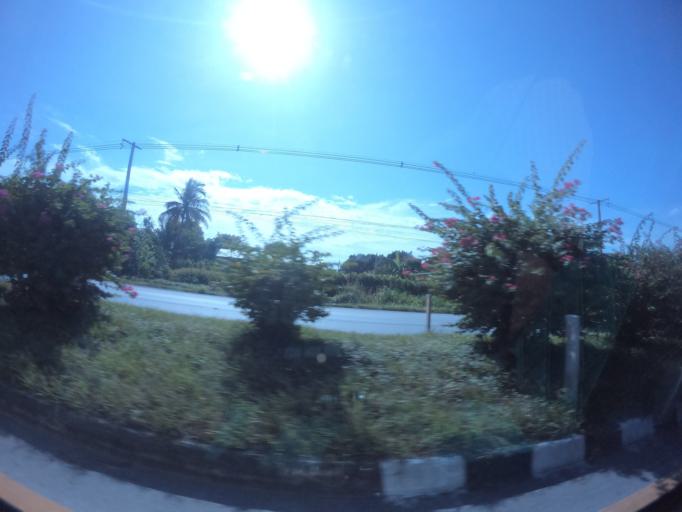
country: TH
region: Nakhon Nayok
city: Ban Na
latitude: 14.2206
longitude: 101.0697
